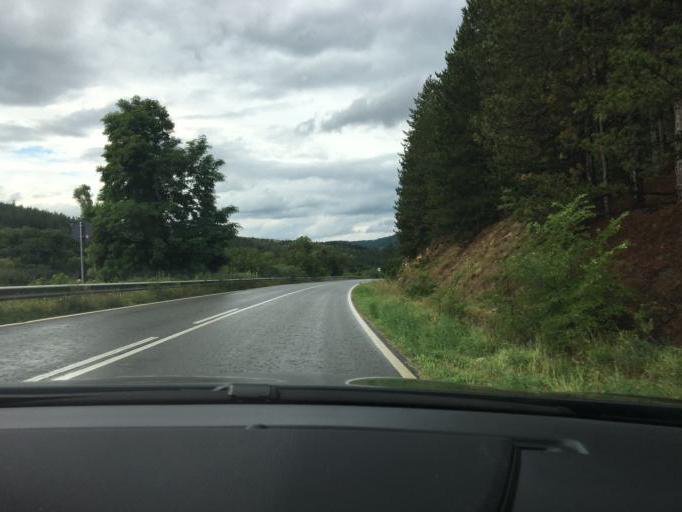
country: BG
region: Kyustendil
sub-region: Obshtina Boboshevo
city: Boboshevo
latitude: 42.2537
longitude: 22.9127
